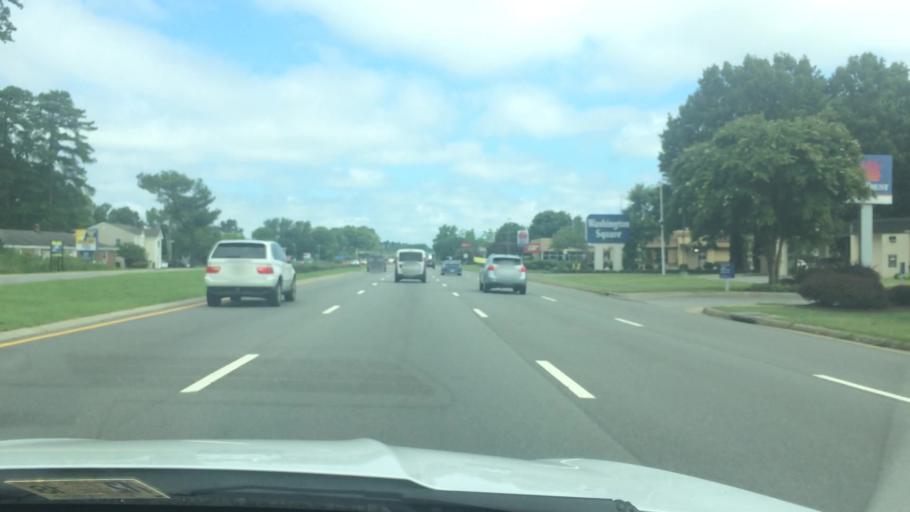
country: US
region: Virginia
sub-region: York County
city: Yorktown
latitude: 37.1565
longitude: -76.4621
